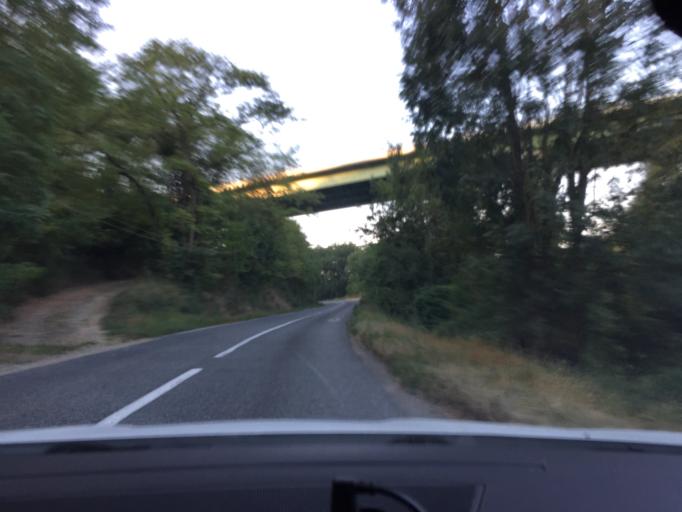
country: FR
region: Rhone-Alpes
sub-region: Departement du Rhone
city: Lozanne
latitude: 45.8524
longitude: 4.6702
